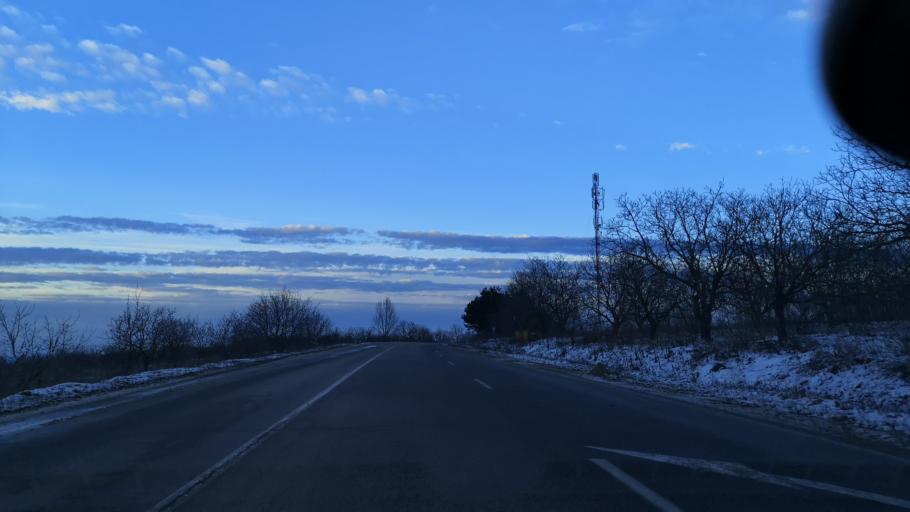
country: MD
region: Orhei
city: Orhei
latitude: 47.5335
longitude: 28.7938
